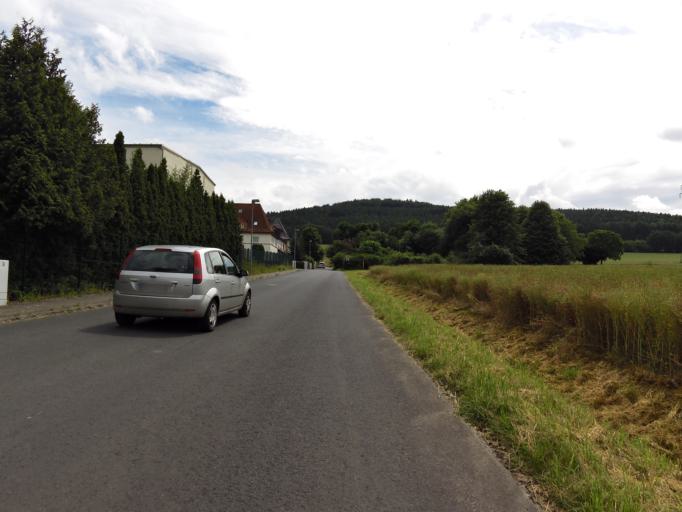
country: DE
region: Thuringia
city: Stadtlengsfeld
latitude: 50.8185
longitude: 10.1202
